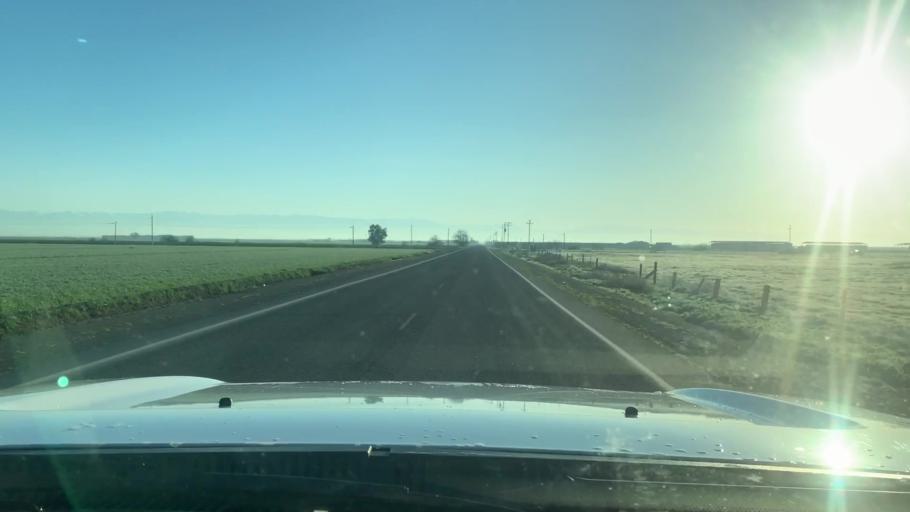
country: US
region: California
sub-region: Kings County
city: Corcoran
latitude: 36.2110
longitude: -119.5676
